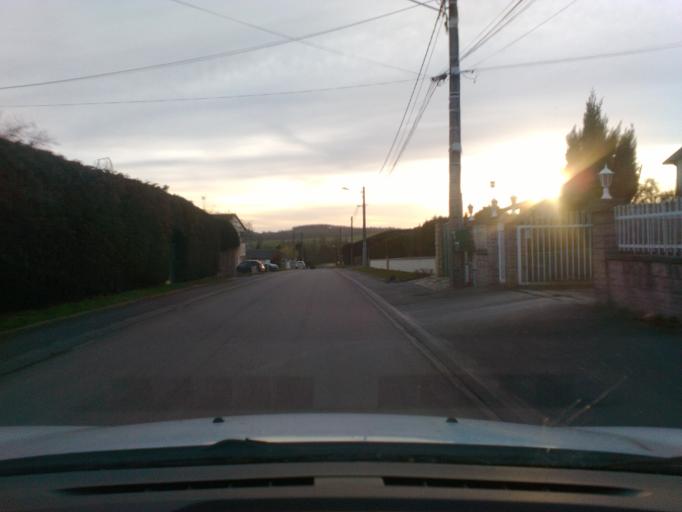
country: FR
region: Lorraine
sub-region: Departement des Vosges
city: Charmes
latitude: 48.3637
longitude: 6.2569
